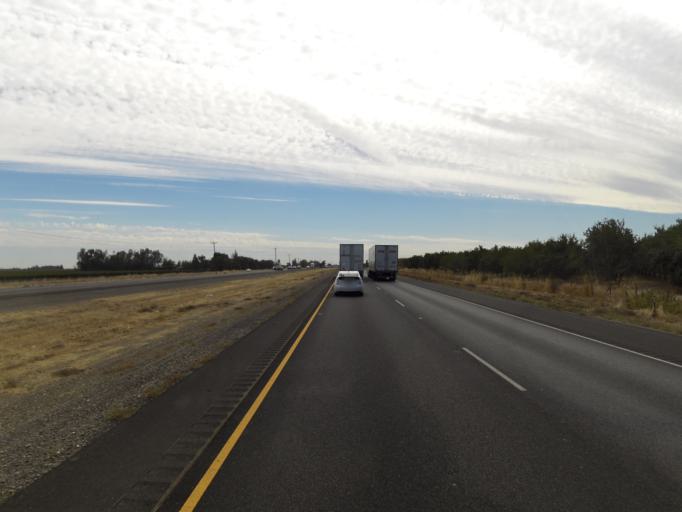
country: US
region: California
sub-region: Colusa County
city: Arbuckle
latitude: 39.0011
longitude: -122.0467
